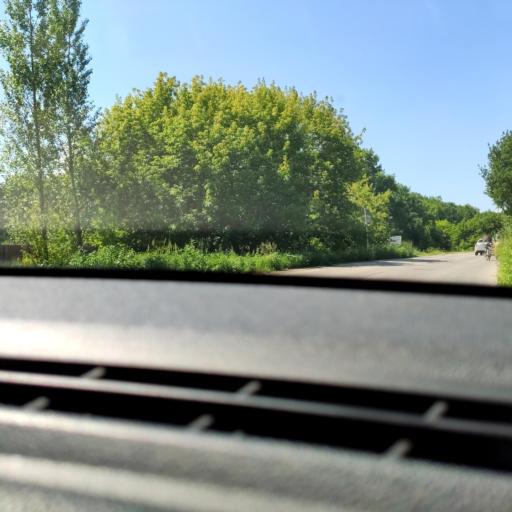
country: RU
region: Samara
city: Podstepki
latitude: 53.5770
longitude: 49.0603
